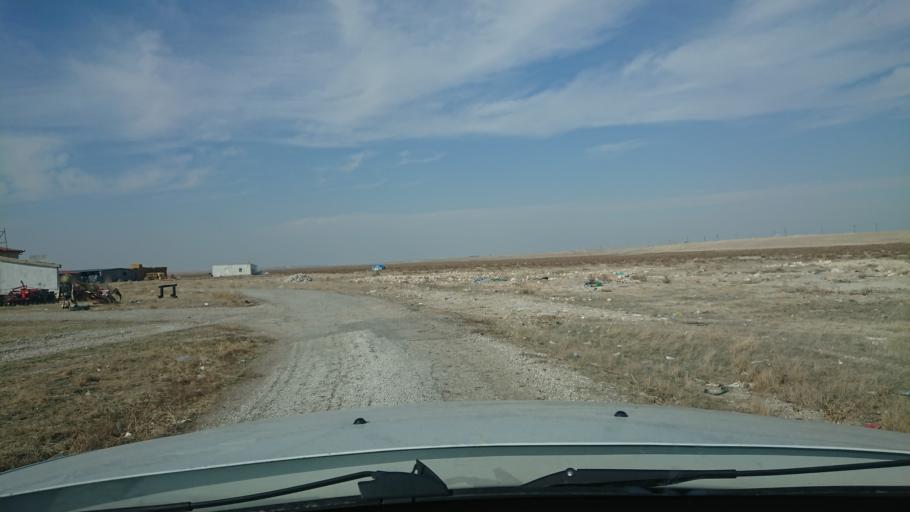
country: TR
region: Aksaray
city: Sultanhani
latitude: 38.2601
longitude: 33.4745
